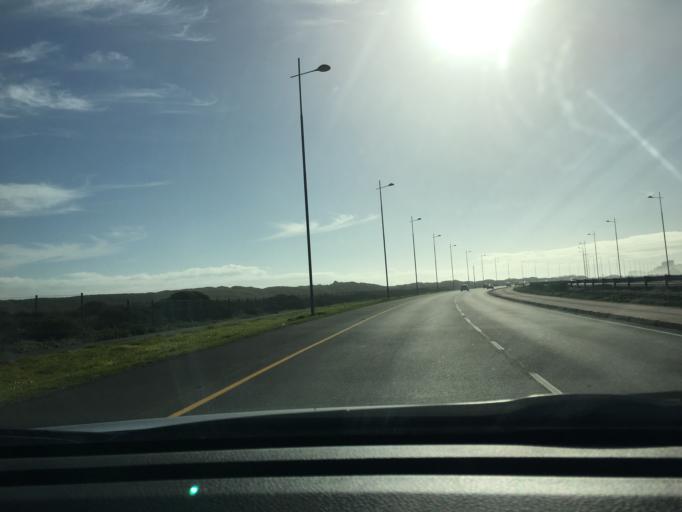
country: ZA
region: Western Cape
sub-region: City of Cape Town
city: Sunset Beach
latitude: -33.8462
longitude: 18.4897
